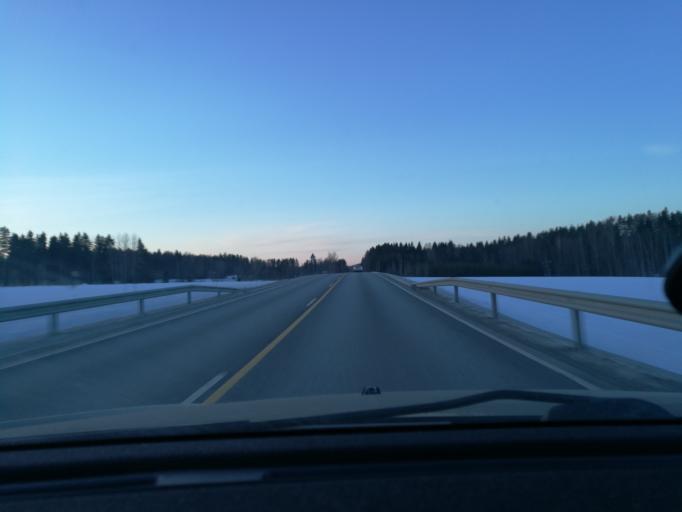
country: FI
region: Uusimaa
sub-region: Helsinki
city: Vihti
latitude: 60.4194
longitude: 24.4415
